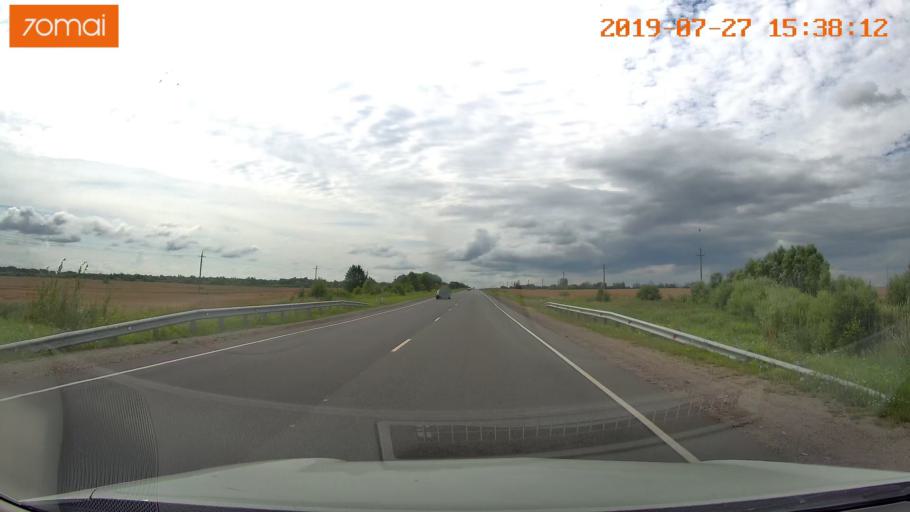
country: RU
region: Kaliningrad
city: Gusev
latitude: 54.6084
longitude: 22.3209
